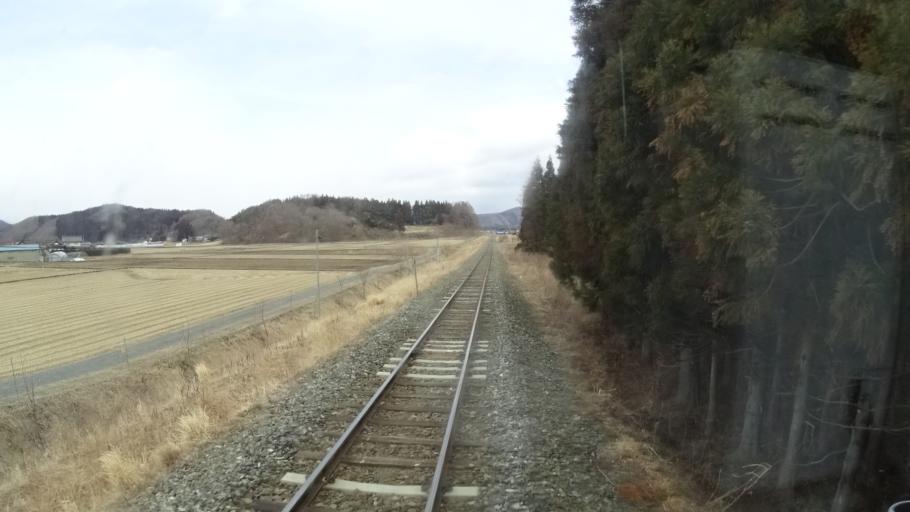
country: JP
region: Iwate
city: Tono
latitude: 39.2724
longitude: 141.5898
